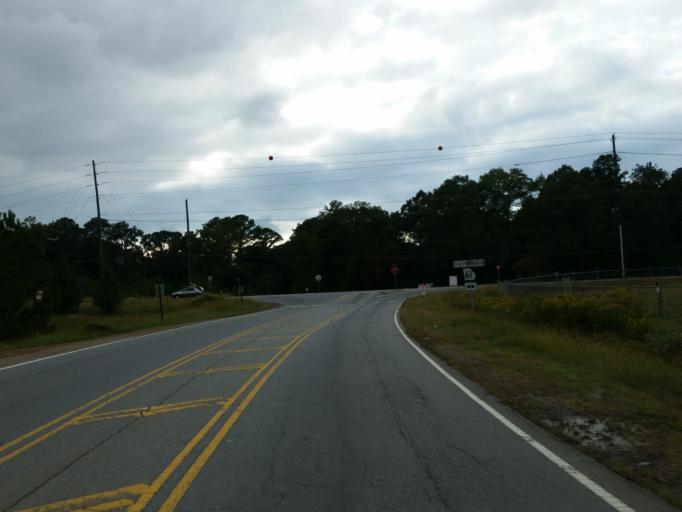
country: US
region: Georgia
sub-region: Bartow County
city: Cartersville
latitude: 34.1131
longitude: -84.8502
